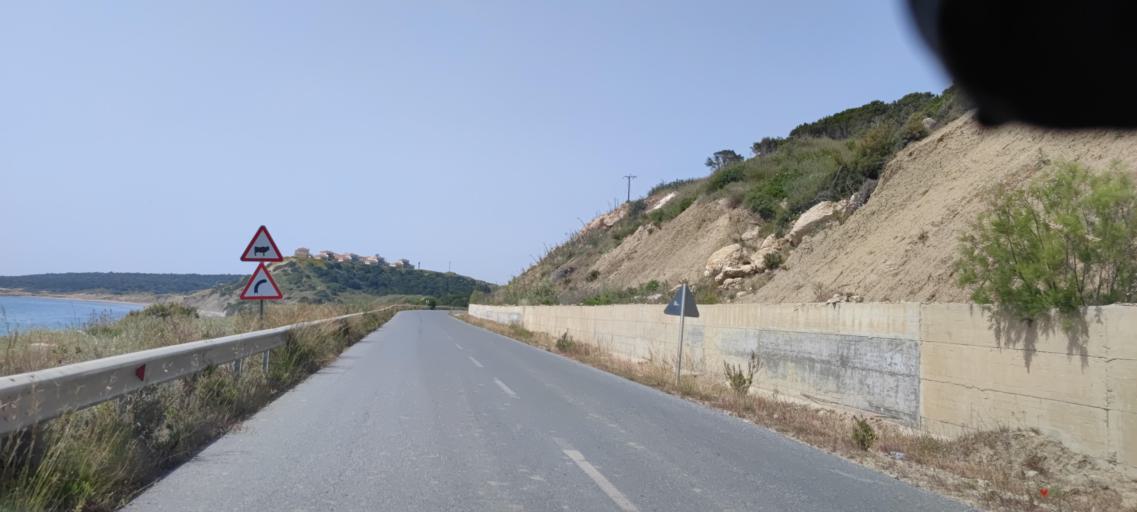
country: CY
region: Ammochostos
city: Rizokarpaso
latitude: 35.5837
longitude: 34.4187
